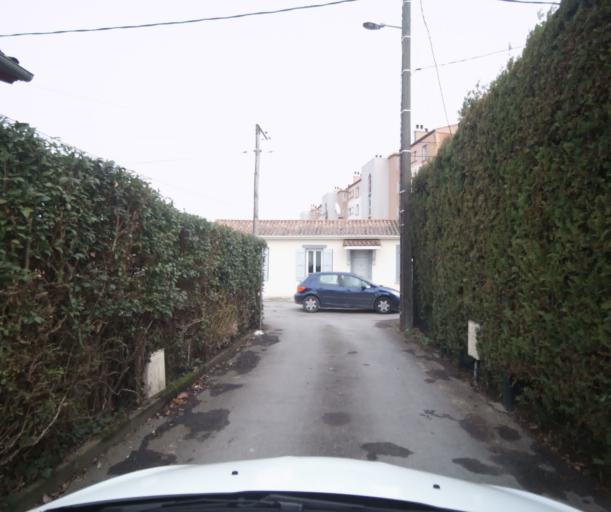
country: FR
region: Midi-Pyrenees
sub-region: Departement du Tarn-et-Garonne
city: Castelsarrasin
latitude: 44.0362
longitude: 1.1161
